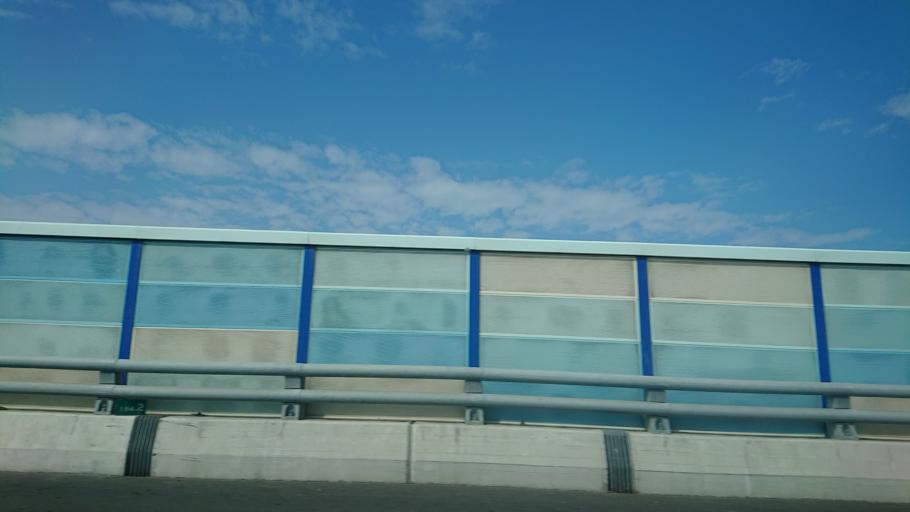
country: TW
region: Taiwan
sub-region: Changhua
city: Chang-hua
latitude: 23.9613
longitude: 120.3360
